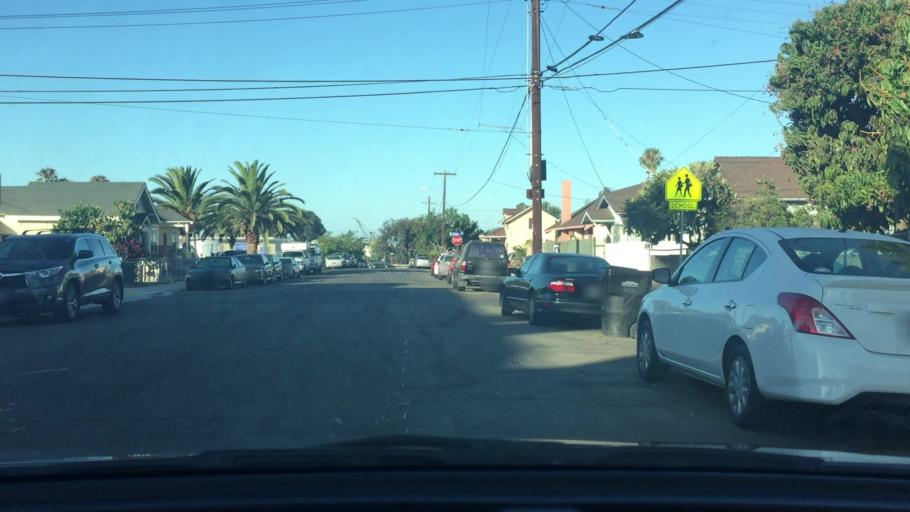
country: US
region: California
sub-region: San Diego County
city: San Diego
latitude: 32.6991
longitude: -117.1356
